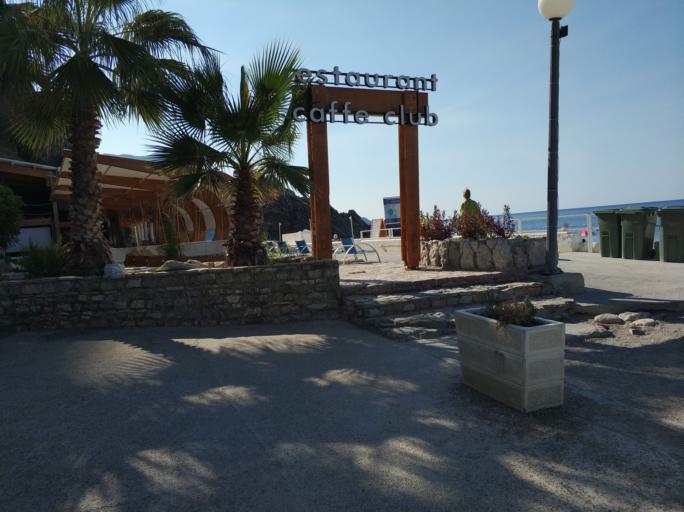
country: ME
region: Budva
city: Budva
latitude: 42.2775
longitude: 18.8808
